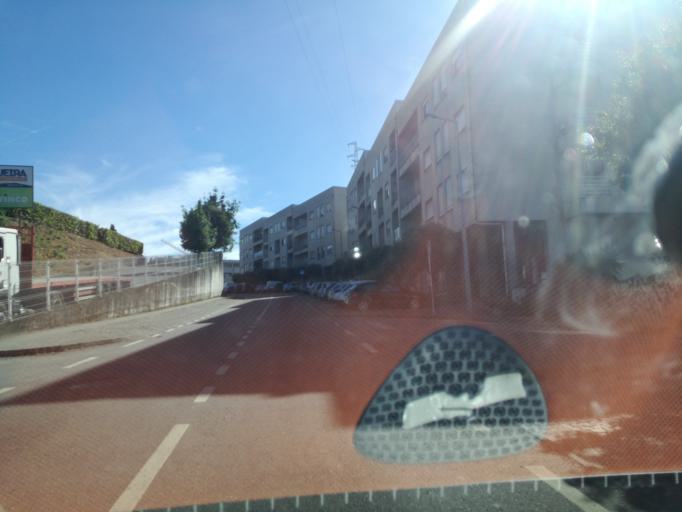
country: PT
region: Braga
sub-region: Guimaraes
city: Guimaraes
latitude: 41.4580
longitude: -8.2953
